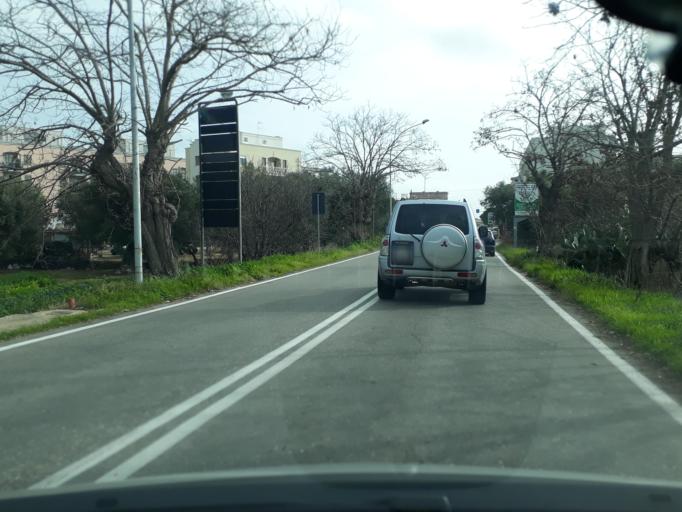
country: IT
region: Apulia
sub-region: Provincia di Bari
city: Monopoli
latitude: 40.9519
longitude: 17.2863
